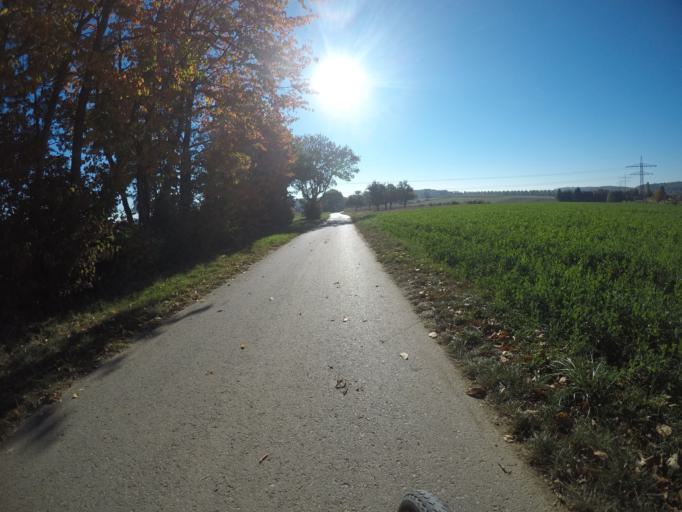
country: DE
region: Baden-Wuerttemberg
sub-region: Regierungsbezirk Stuttgart
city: Leinfelden-Echterdingen
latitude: 48.6979
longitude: 9.1537
